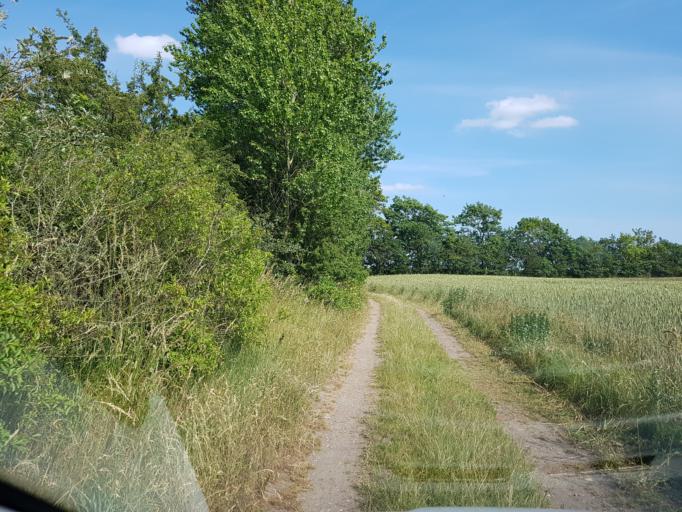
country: DK
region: South Denmark
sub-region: Esbjerg Kommune
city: Ribe
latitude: 55.3886
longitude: 8.7383
